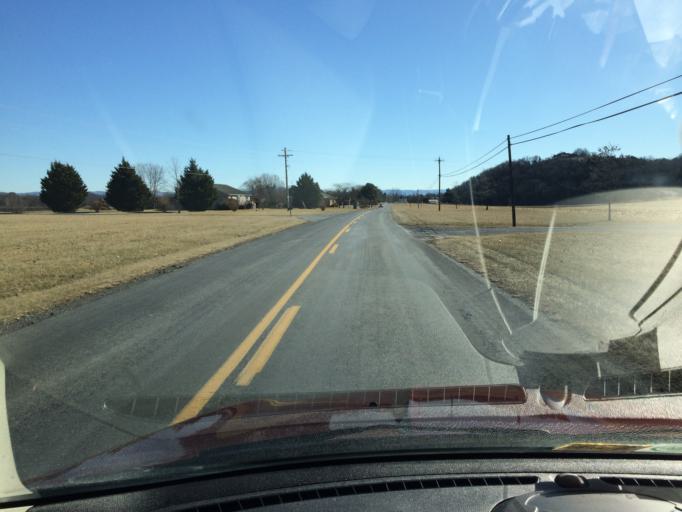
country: US
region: Virginia
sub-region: Rockingham County
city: Bridgewater
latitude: 38.3614
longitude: -78.9597
